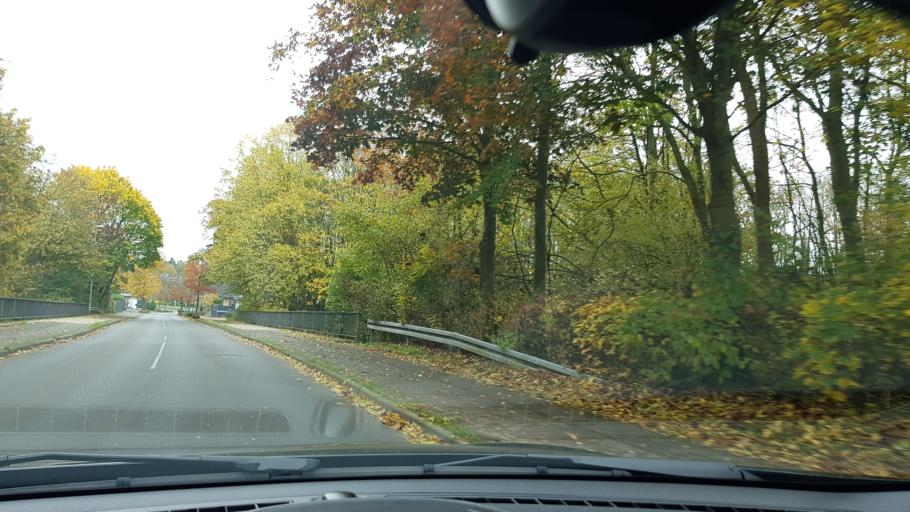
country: DE
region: North Rhine-Westphalia
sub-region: Regierungsbezirk Koln
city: Bedburg
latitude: 50.9984
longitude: 6.5583
